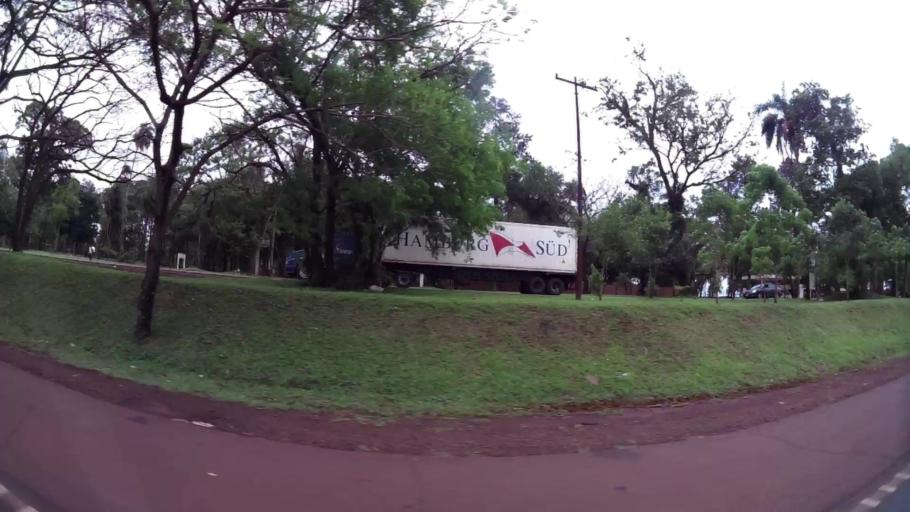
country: PY
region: Alto Parana
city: Ciudad del Este
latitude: -25.4951
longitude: -54.6952
